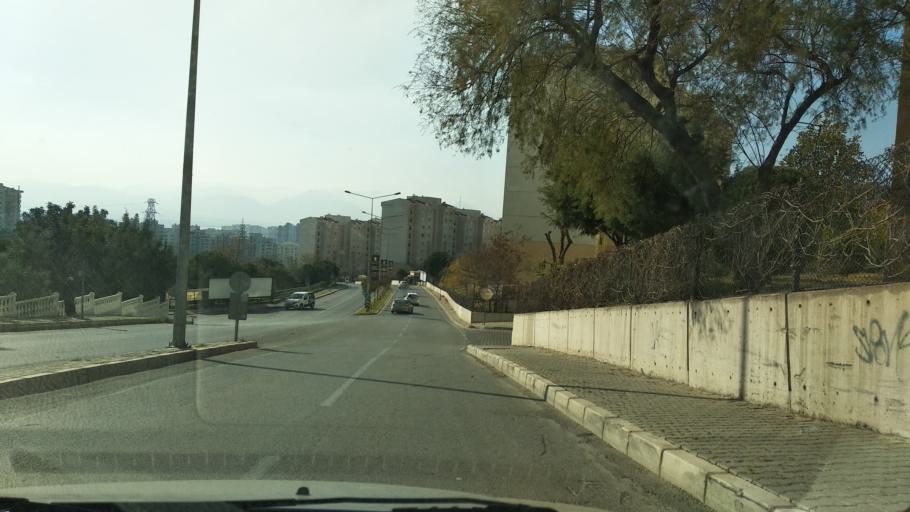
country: TR
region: Izmir
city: Karsiyaka
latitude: 38.4931
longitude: 27.0923
